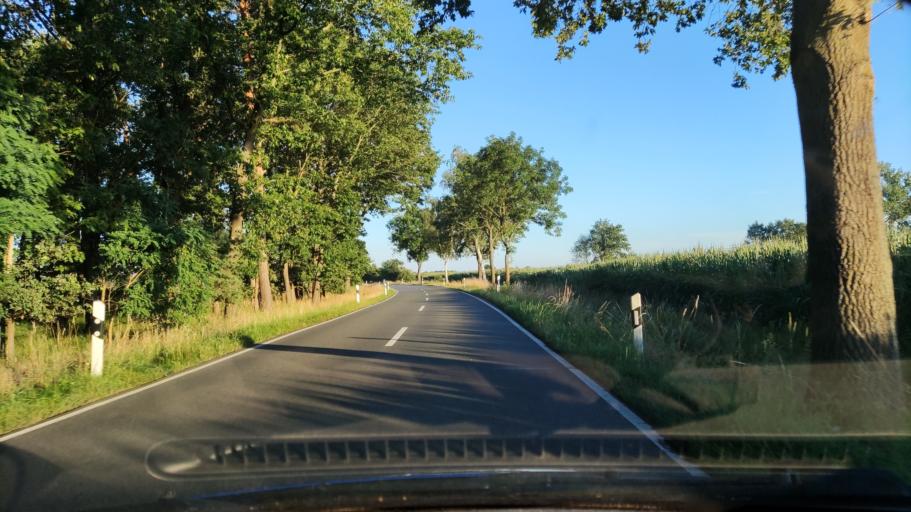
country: DE
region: Lower Saxony
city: Luechow
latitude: 53.0150
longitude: 11.1501
